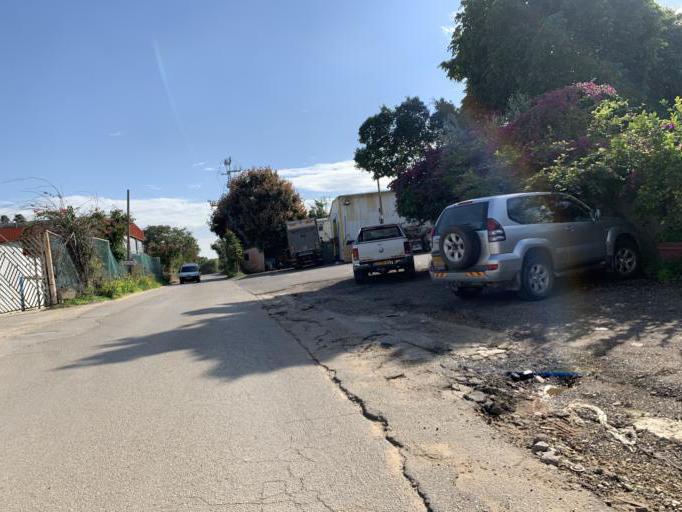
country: IL
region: Central District
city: Ra'anana
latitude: 32.1685
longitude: 34.8788
